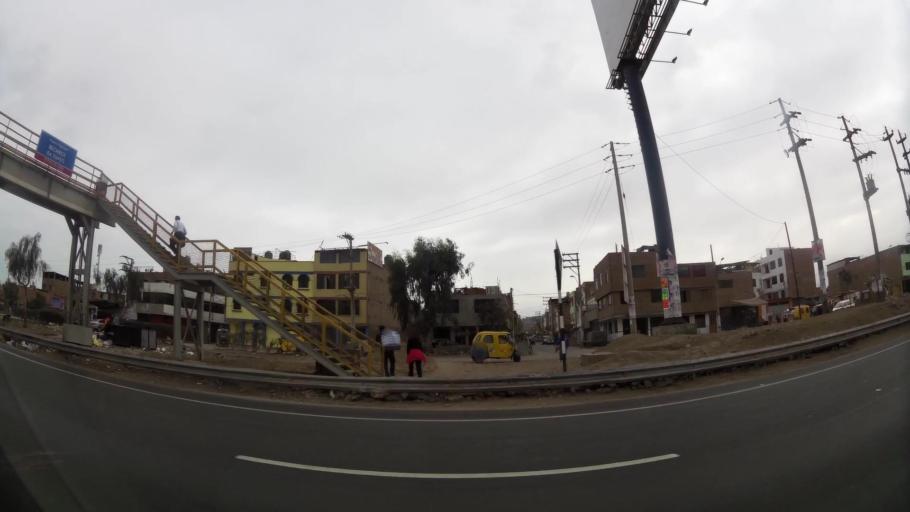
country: PE
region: Lima
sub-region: Lima
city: Surco
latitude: -12.1877
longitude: -76.9739
